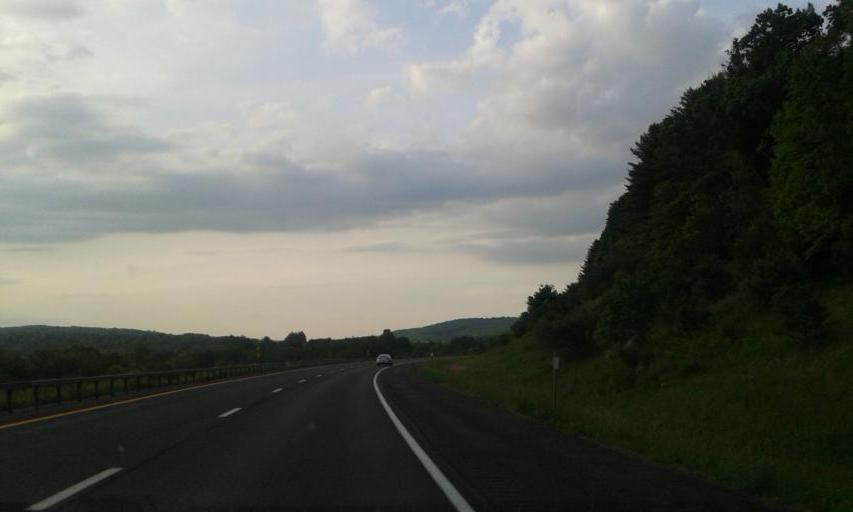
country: US
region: New York
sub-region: Broome County
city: Chenango Bridge
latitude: 42.1837
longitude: -75.9018
